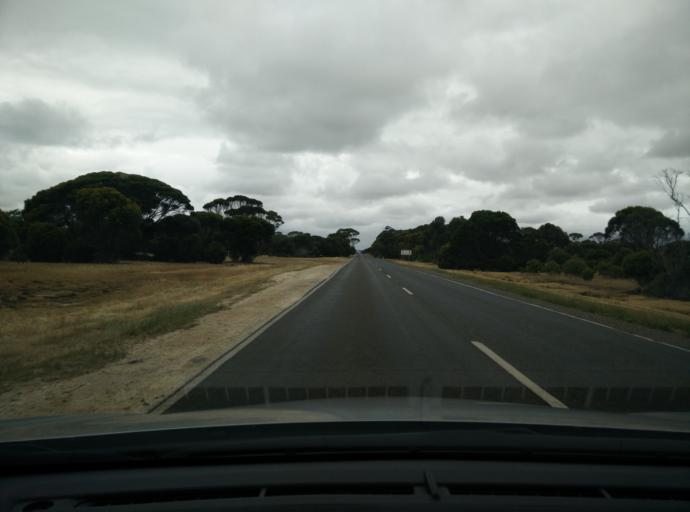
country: AU
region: South Australia
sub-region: Kangaroo Island
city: Kingscote
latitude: -35.6810
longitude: 137.5731
